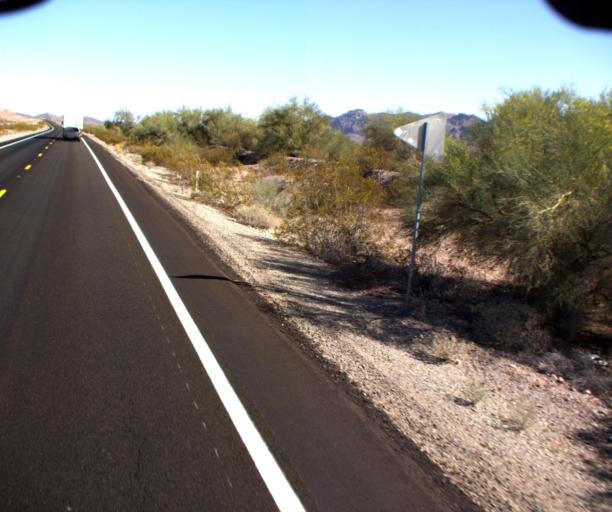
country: US
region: Arizona
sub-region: La Paz County
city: Quartzsite
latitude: 33.1673
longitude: -114.2777
